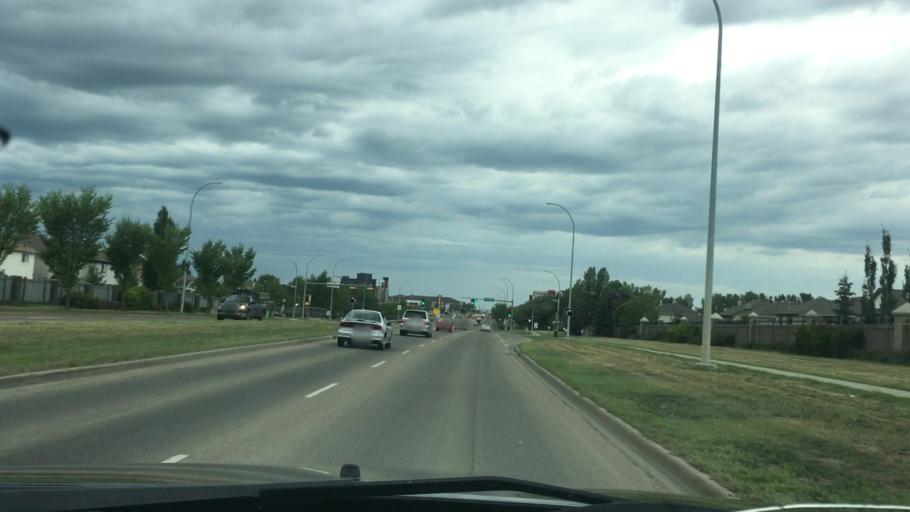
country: CA
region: Alberta
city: Beaumont
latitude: 53.4249
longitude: -113.5066
